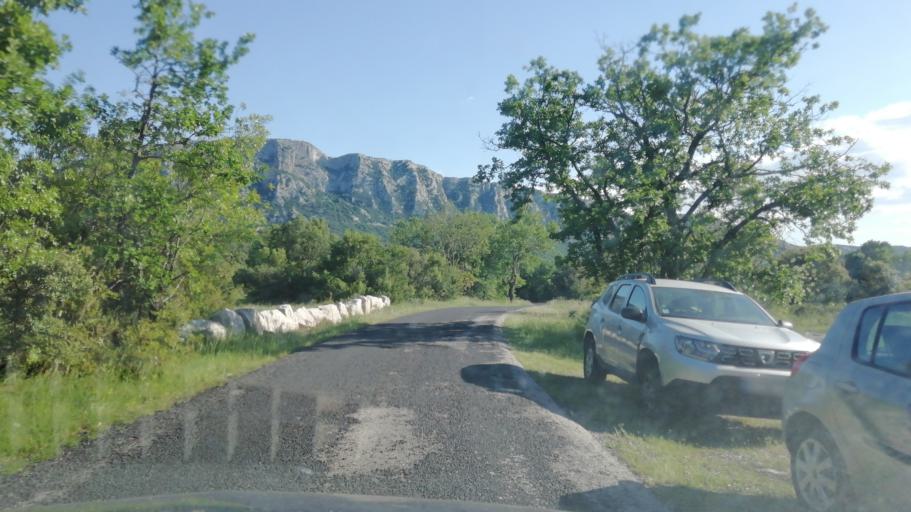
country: FR
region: Languedoc-Roussillon
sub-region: Departement de l'Herault
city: Saint-Mathieu-de-Treviers
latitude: 43.7973
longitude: 3.8111
